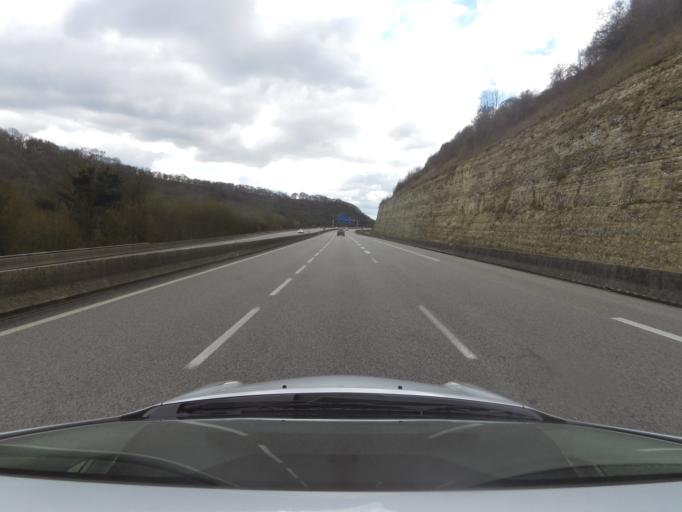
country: FR
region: Haute-Normandie
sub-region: Departement de la Seine-Maritime
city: Rogerville
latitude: 49.5044
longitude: 0.2796
